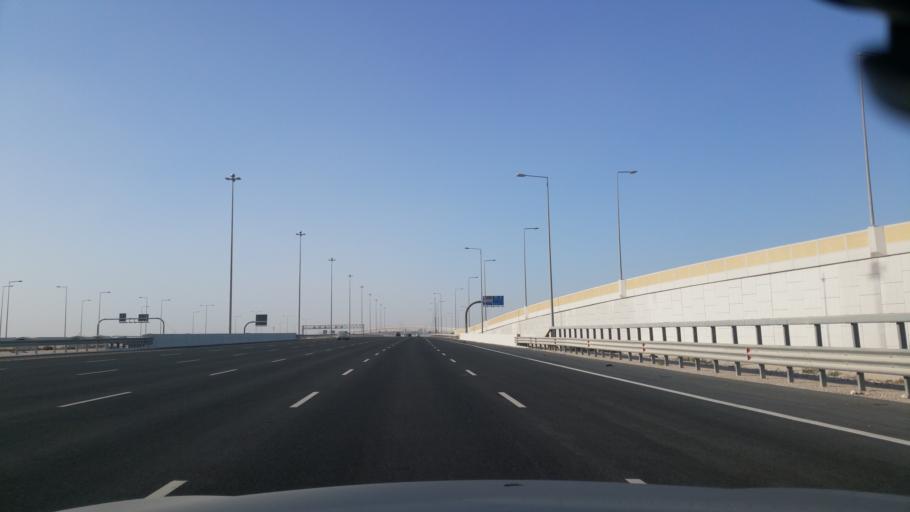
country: QA
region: Al Wakrah
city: Al Wukayr
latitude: 25.1881
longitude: 51.5466
